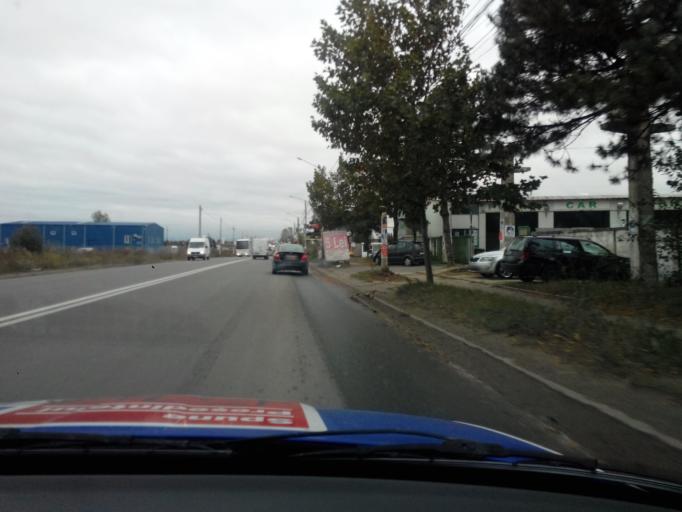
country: RO
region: Ilfov
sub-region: Comuna Jilava
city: Jilava
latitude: 44.3514
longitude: 26.0846
